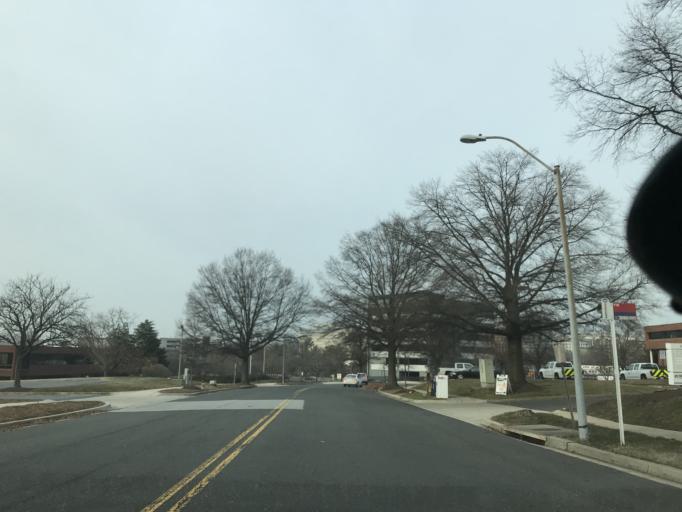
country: US
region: Maryland
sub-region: Prince George's County
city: Lanham
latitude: 38.9498
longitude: -76.8641
